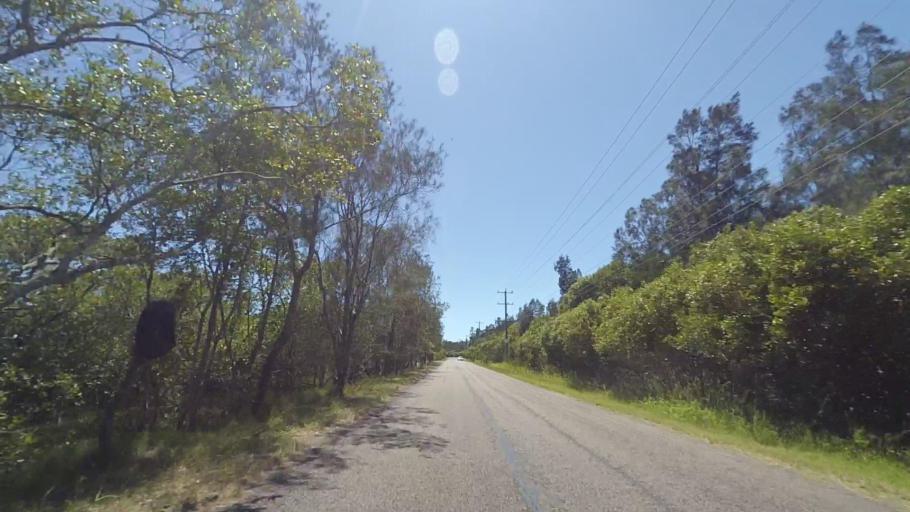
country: AU
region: New South Wales
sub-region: Port Stephens Shire
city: Medowie
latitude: -32.7786
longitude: 151.9635
